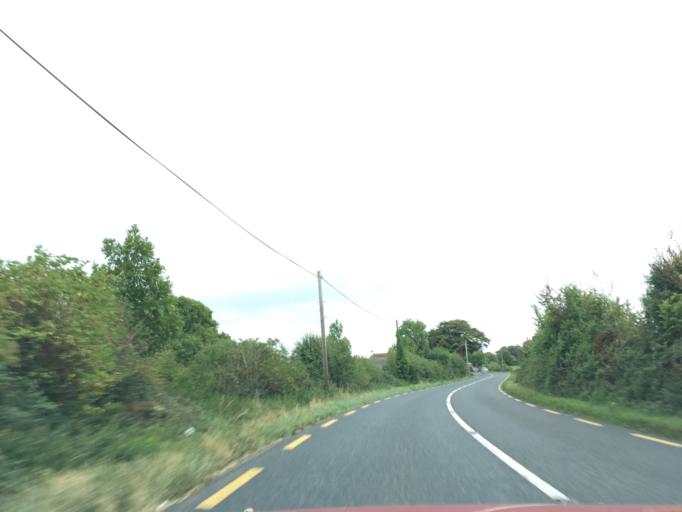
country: IE
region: Munster
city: Cashel
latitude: 52.4429
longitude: -7.8010
